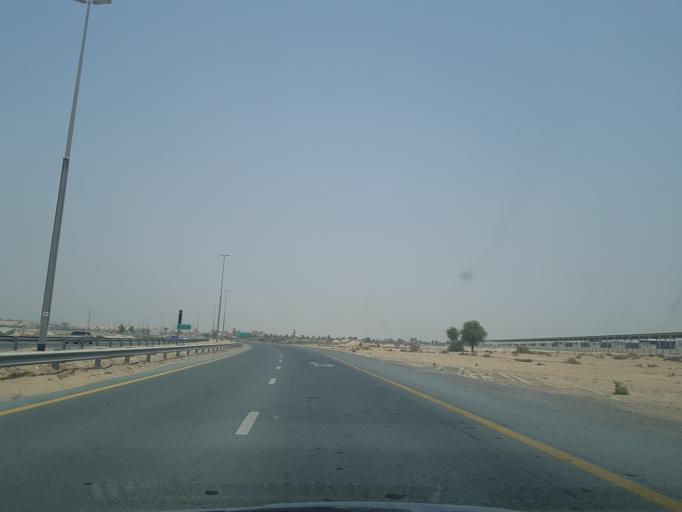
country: AE
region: Ash Shariqah
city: Sharjah
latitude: 25.1615
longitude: 55.4573
